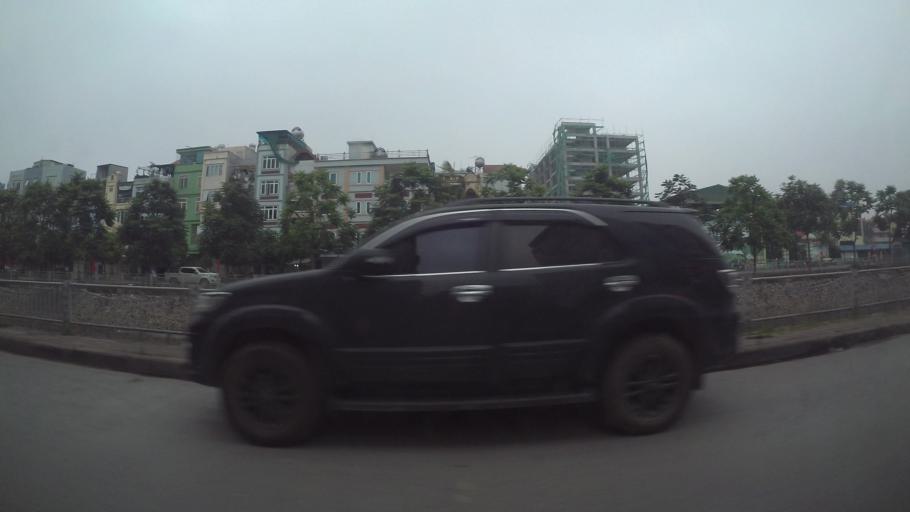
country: VN
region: Ha Noi
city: Hai BaTrung
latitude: 20.9918
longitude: 105.8367
